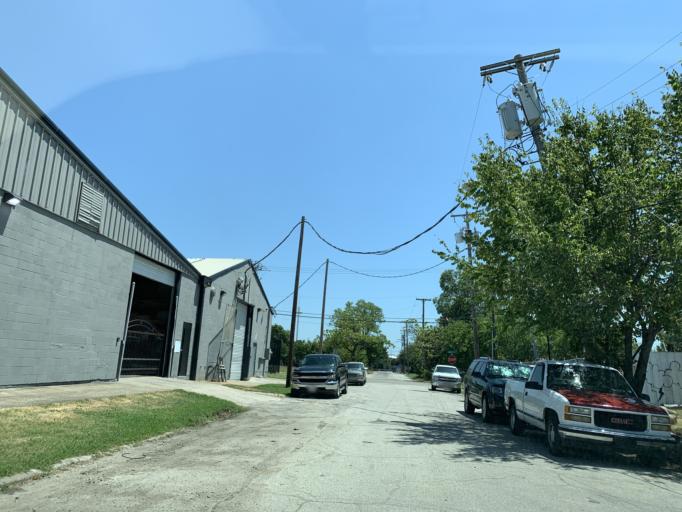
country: US
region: Texas
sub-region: Dallas County
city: Dallas
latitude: 32.7793
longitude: -96.7701
